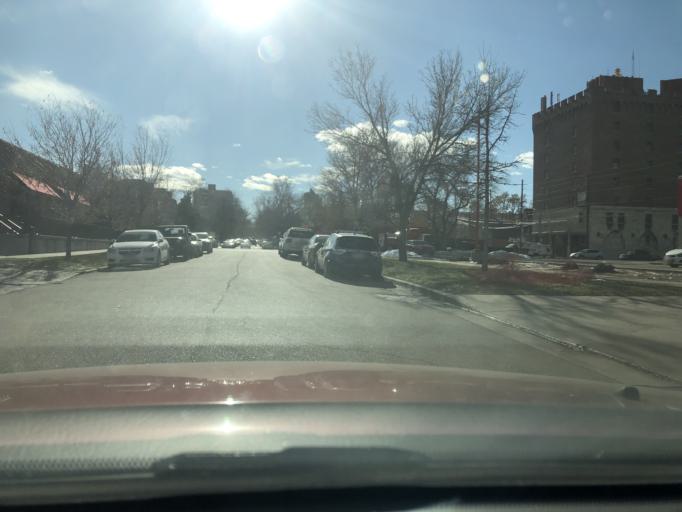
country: US
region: Colorado
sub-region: Denver County
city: Denver
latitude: 39.7407
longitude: -104.9610
